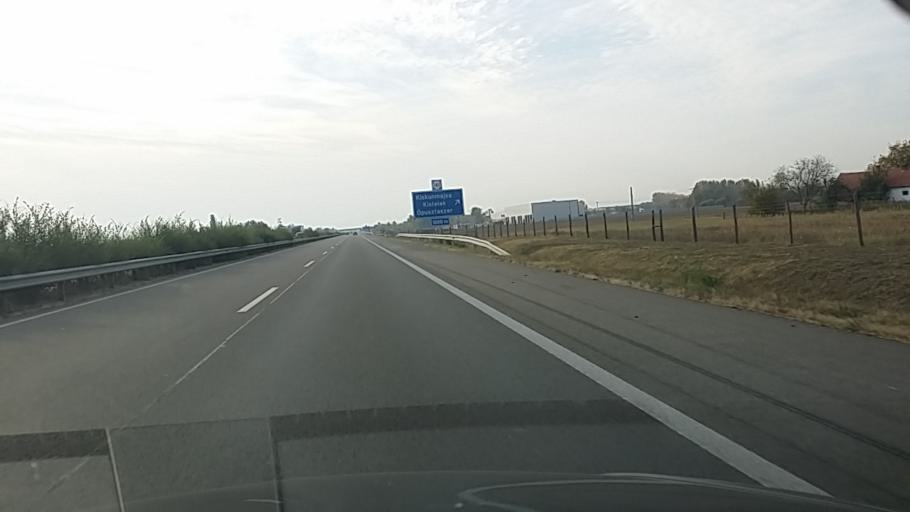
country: HU
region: Csongrad
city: Kistelek
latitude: 46.4768
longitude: 19.9230
